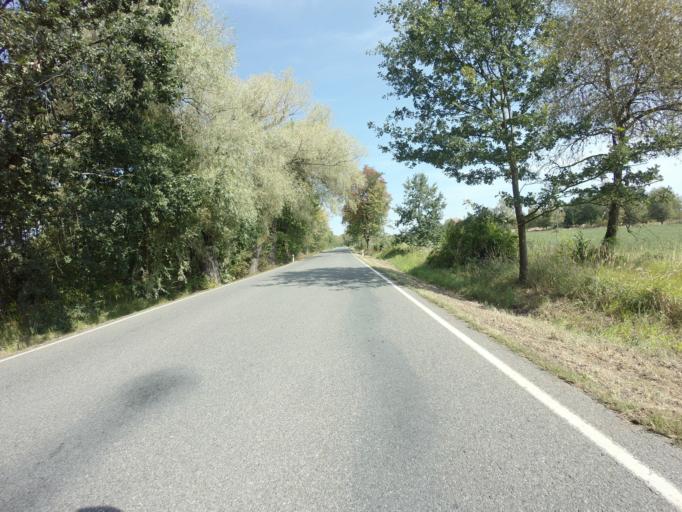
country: CZ
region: Central Bohemia
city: Sedlcany
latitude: 49.6071
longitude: 14.3844
